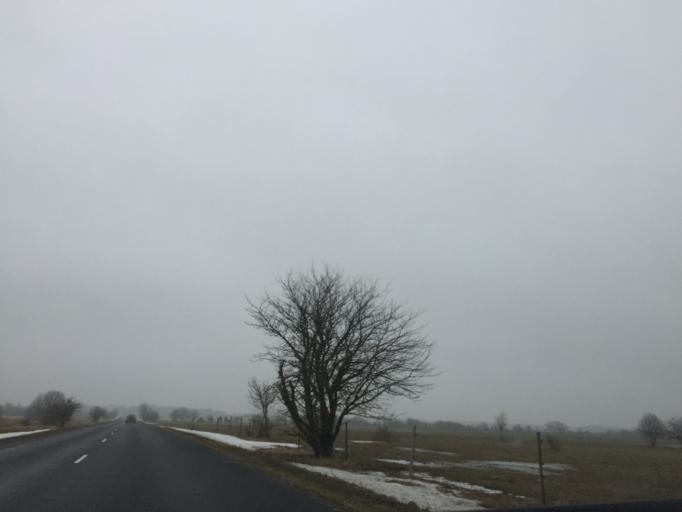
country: EE
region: Saare
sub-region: Kuressaare linn
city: Kuressaare
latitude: 58.2969
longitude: 22.8052
